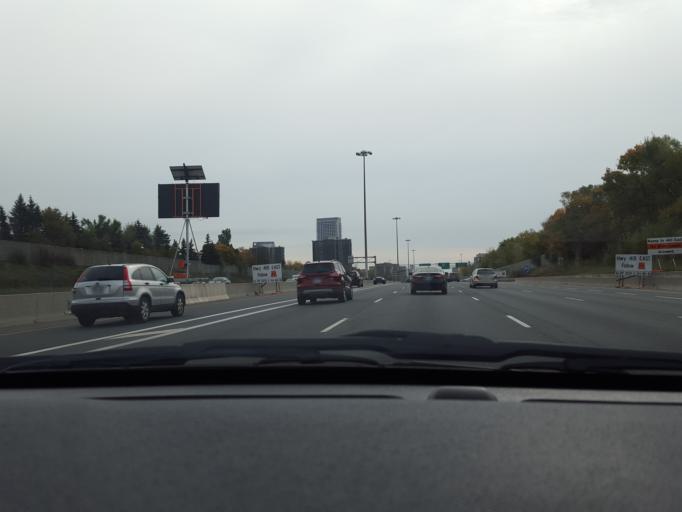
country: CA
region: Ontario
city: Willowdale
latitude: 43.7858
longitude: -79.3416
